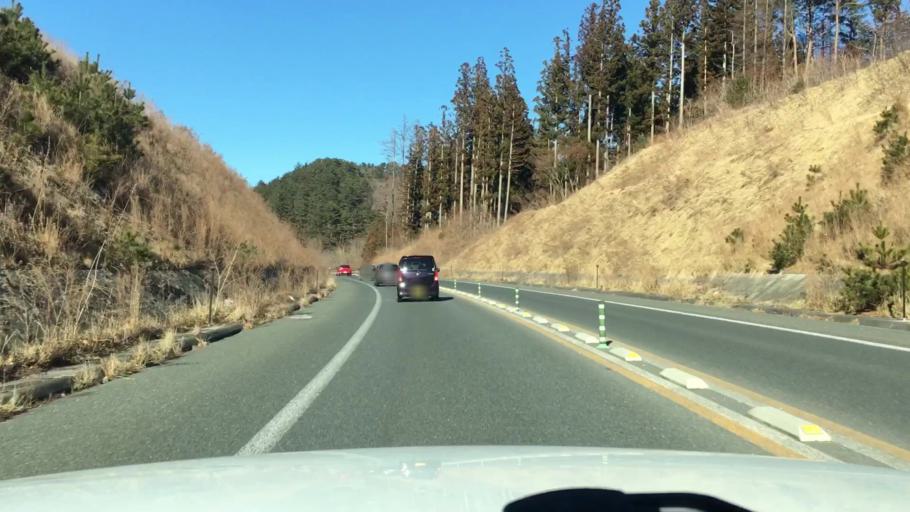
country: JP
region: Iwate
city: Miyako
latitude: 39.6134
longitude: 141.9349
